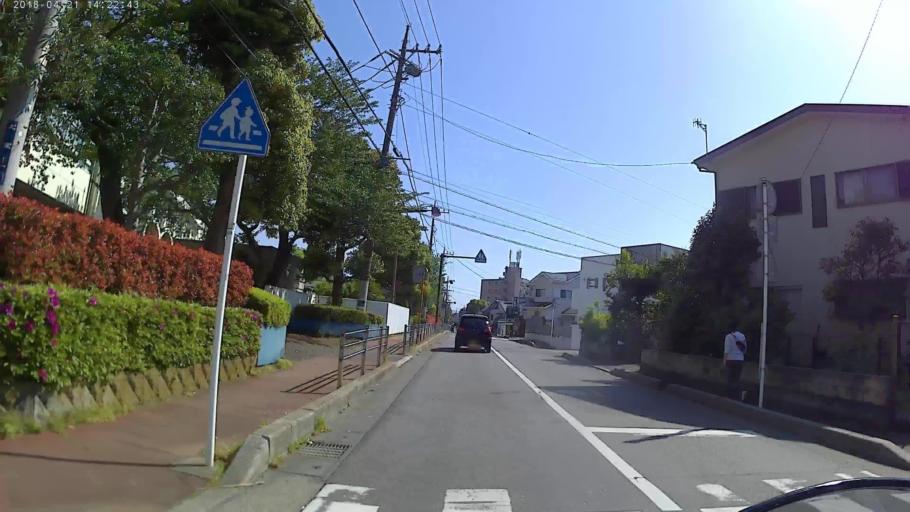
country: JP
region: Kanagawa
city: Hiratsuka
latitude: 35.3446
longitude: 139.3381
